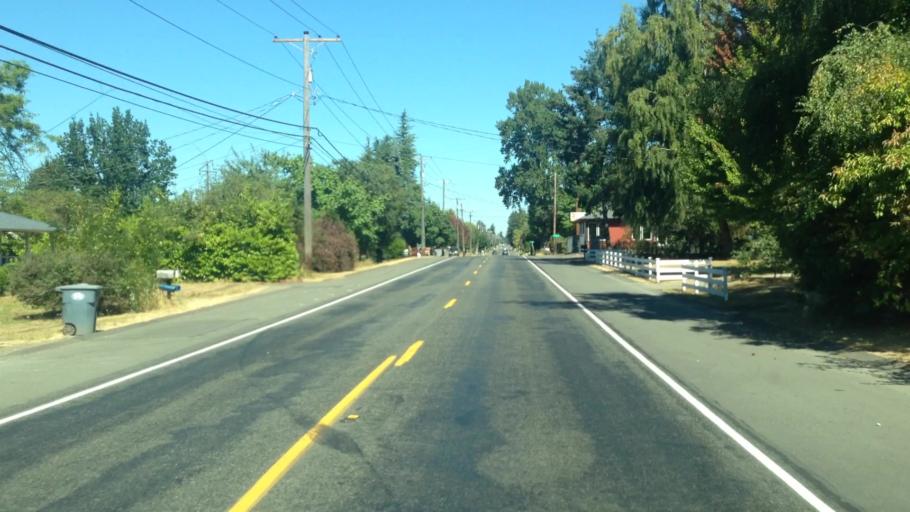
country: US
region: Washington
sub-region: Pierce County
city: Midland
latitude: 47.1683
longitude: -122.4155
